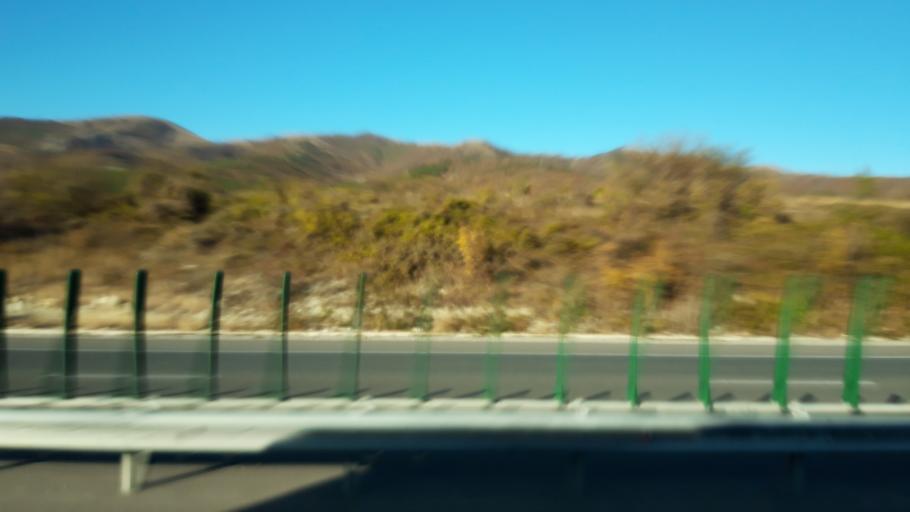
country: RU
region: Krasnodarskiy
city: Kabardinka
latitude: 44.6421
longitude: 37.9739
